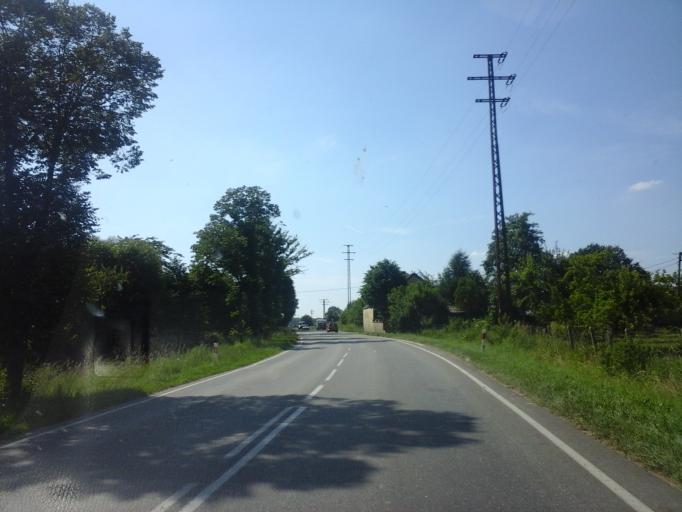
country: PL
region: West Pomeranian Voivodeship
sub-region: Powiat bialogardzki
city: Bialogard
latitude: 54.0227
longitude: 15.9346
